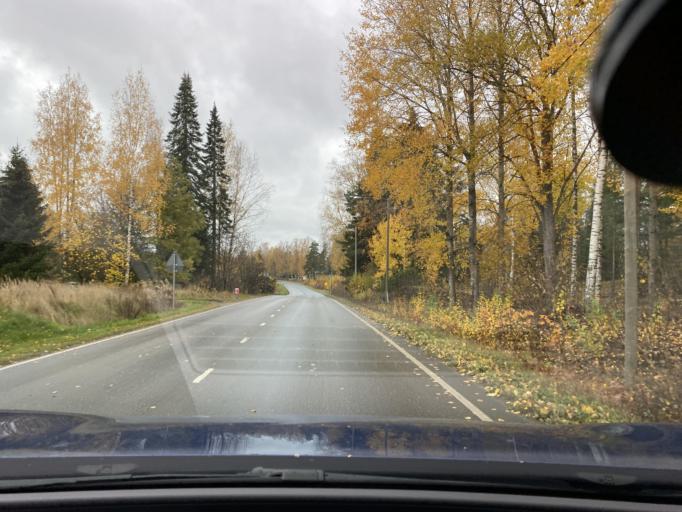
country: FI
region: Satakunta
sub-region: Pori
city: Kokemaeki
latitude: 61.2661
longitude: 22.4059
